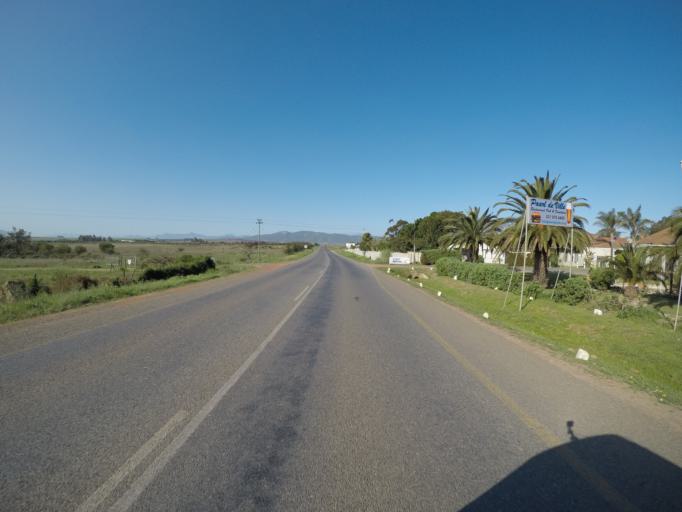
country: ZA
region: Western Cape
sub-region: City of Cape Town
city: Kraaifontein
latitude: -33.7664
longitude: 18.7881
